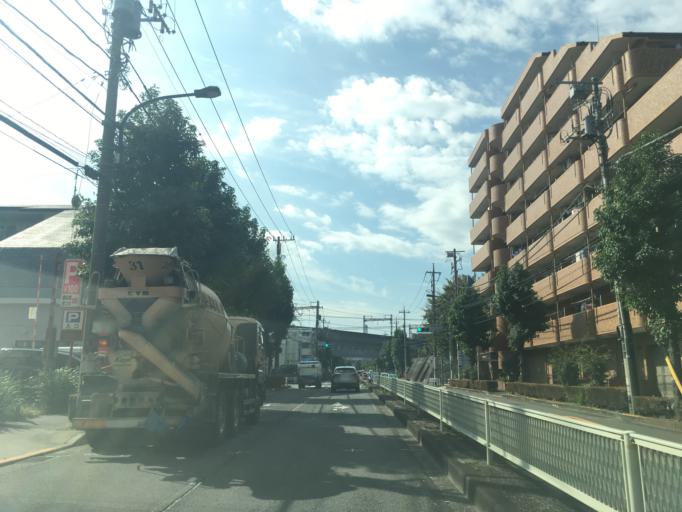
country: JP
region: Tokyo
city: Hino
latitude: 35.6230
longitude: 139.4170
